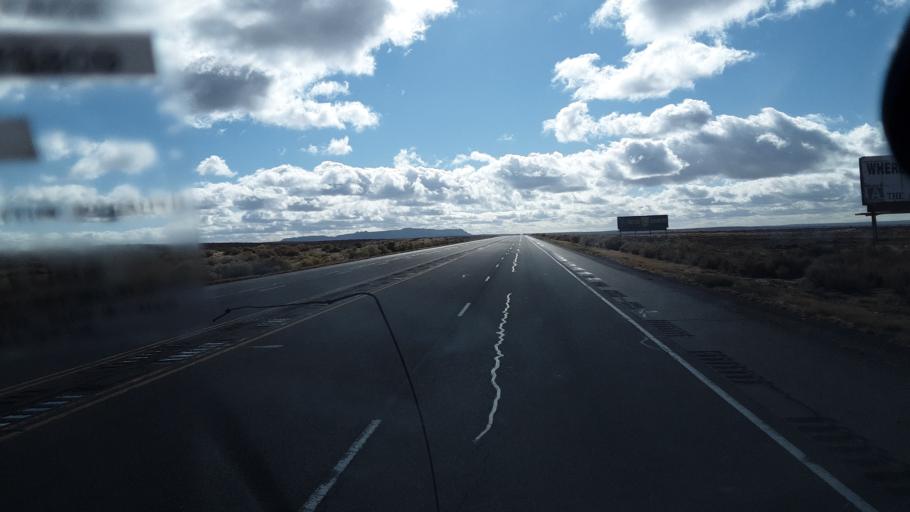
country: US
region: New Mexico
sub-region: San Juan County
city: Bloomfield
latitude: 36.5121
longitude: -107.9434
